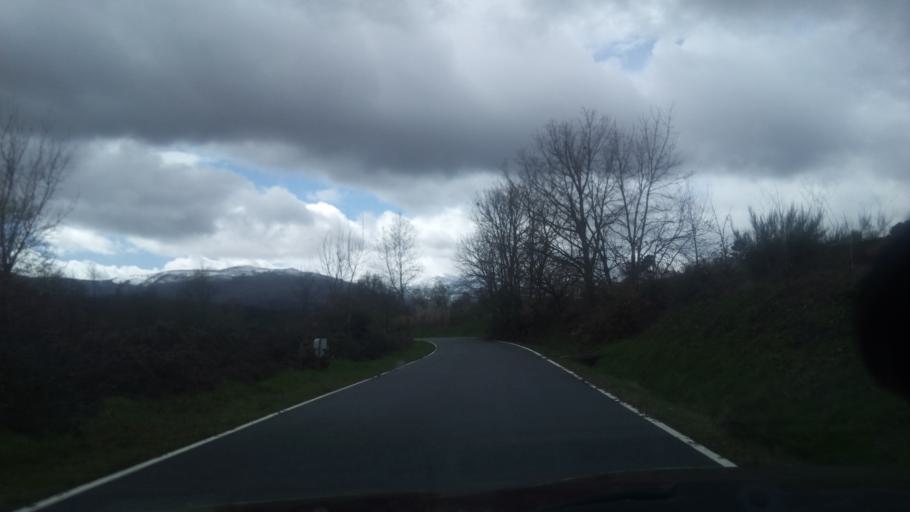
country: PT
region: Guarda
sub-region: Fornos de Algodres
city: Fornos de Algodres
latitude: 40.5700
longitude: -7.4697
